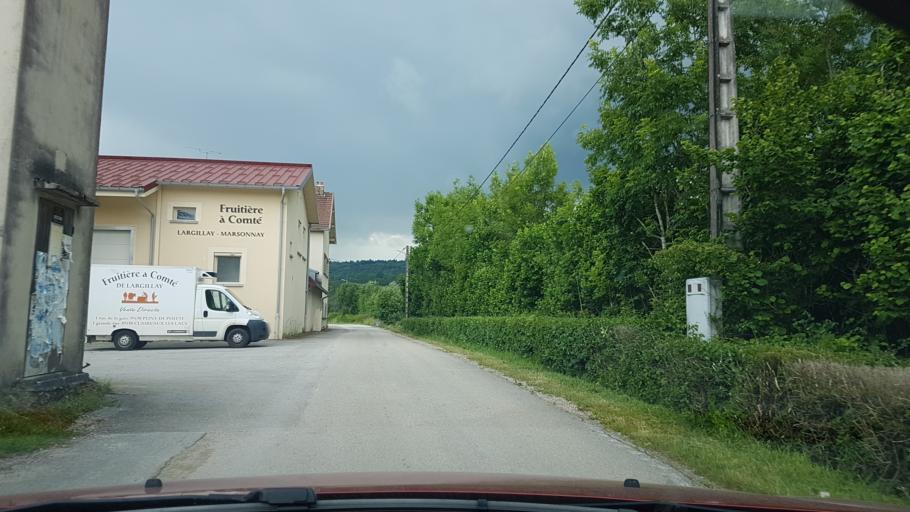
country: FR
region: Franche-Comte
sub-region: Departement du Jura
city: Orgelet
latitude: 46.5540
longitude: 5.6719
